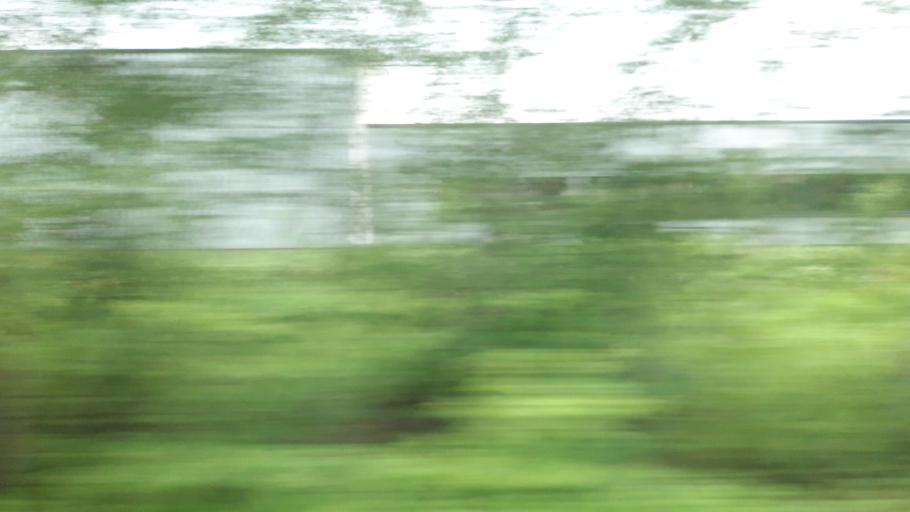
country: DE
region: North Rhine-Westphalia
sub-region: Regierungsbezirk Detmold
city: Hovelhof
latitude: 51.8400
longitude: 8.6510
